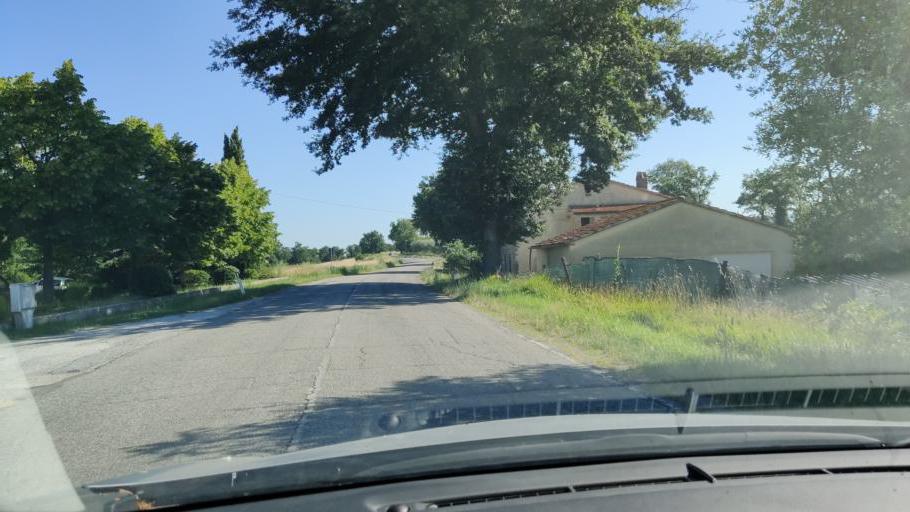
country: IT
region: Umbria
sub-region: Provincia di Terni
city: Avigliano Umbro
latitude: 42.6658
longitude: 12.4406
